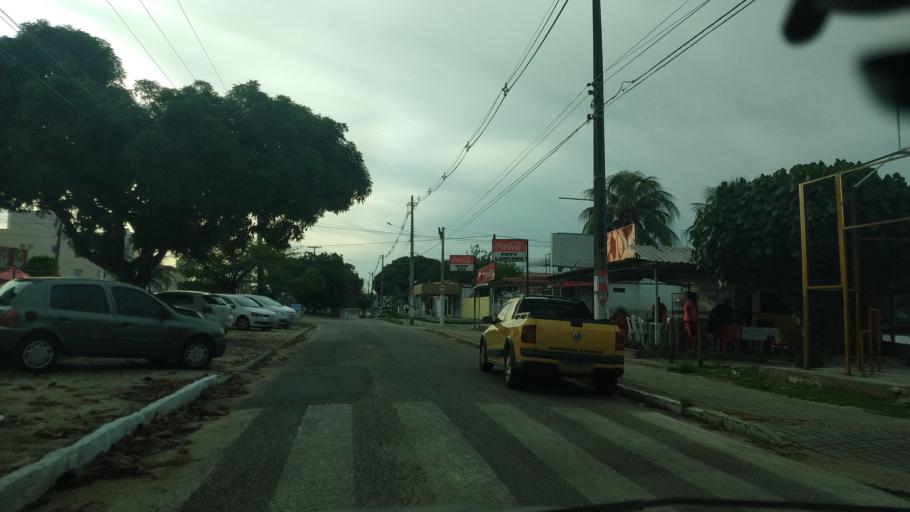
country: BR
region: Rio Grande do Norte
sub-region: Natal
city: Natal
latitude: -5.8302
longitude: -35.2090
